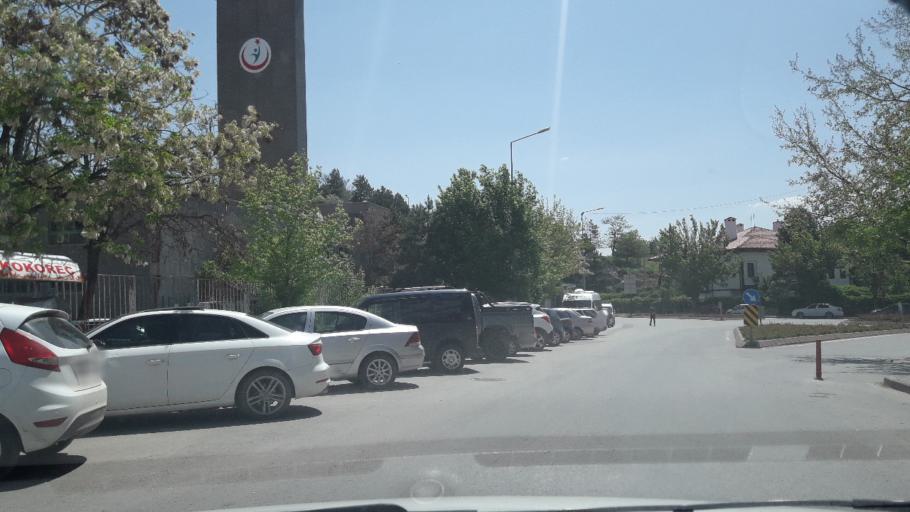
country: TR
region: Sivas
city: Sivas
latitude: 39.7440
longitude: 37.0113
